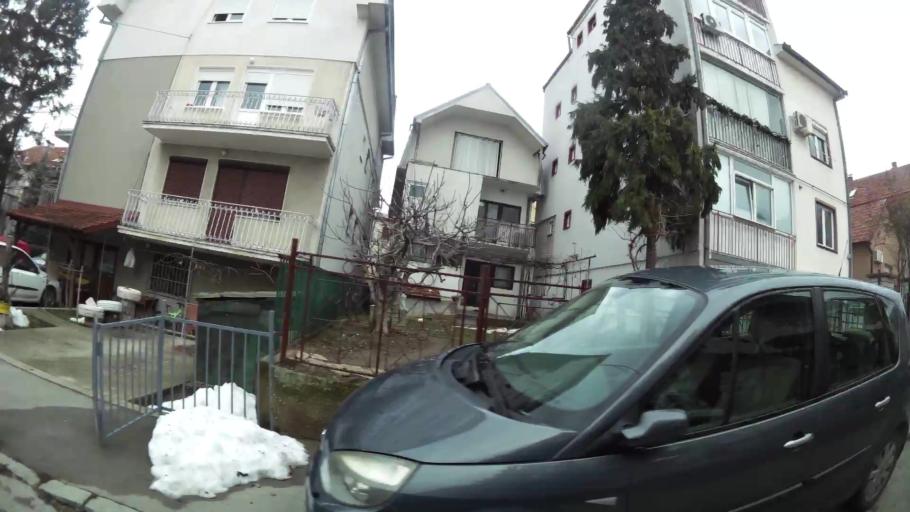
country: RS
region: Central Serbia
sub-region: Belgrade
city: Cukarica
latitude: 44.7599
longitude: 20.4102
